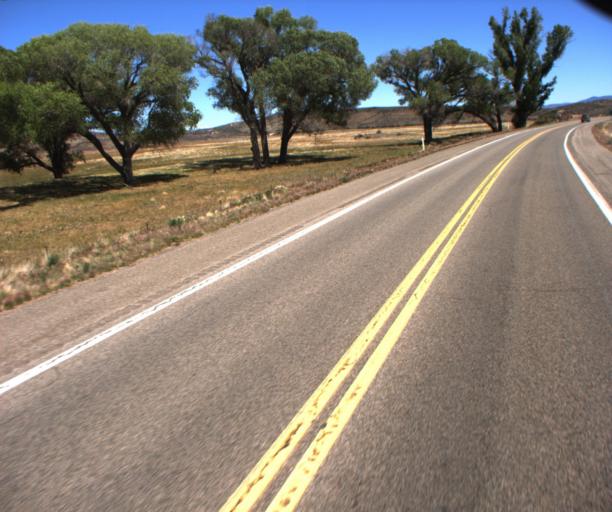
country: US
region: Arizona
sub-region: Yavapai County
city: Congress
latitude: 34.2987
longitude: -112.7226
